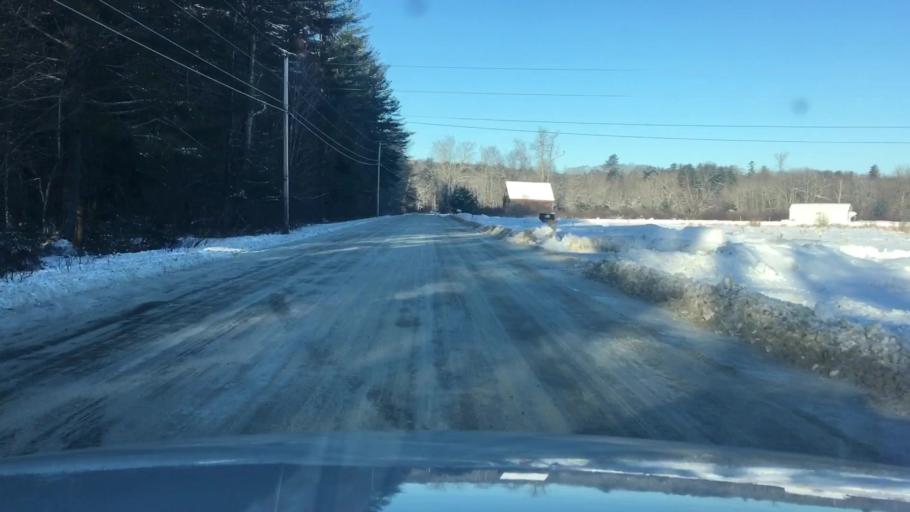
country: US
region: Maine
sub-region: Kennebec County
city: Belgrade
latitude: 44.4289
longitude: -69.8984
